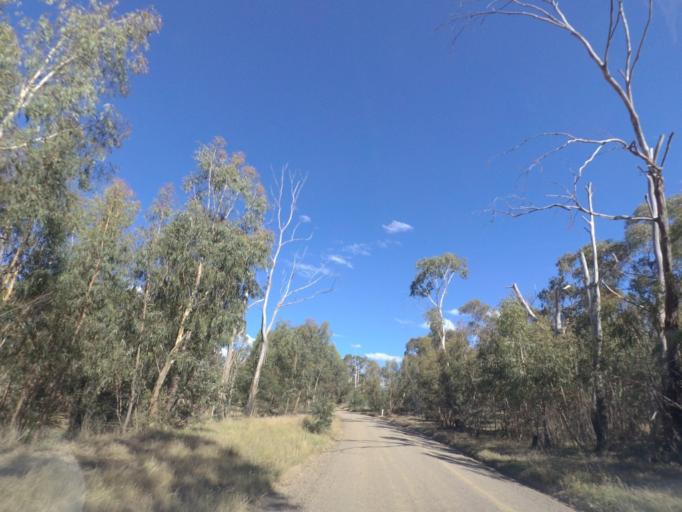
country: AU
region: Victoria
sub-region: Hume
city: Craigieburn
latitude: -37.4266
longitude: 144.9259
